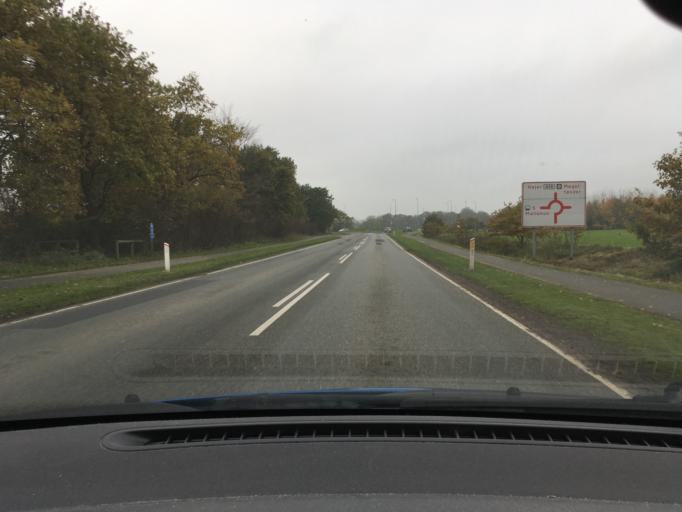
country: DK
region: South Denmark
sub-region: Tonder Kommune
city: Tonder
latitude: 54.9452
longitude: 8.8469
